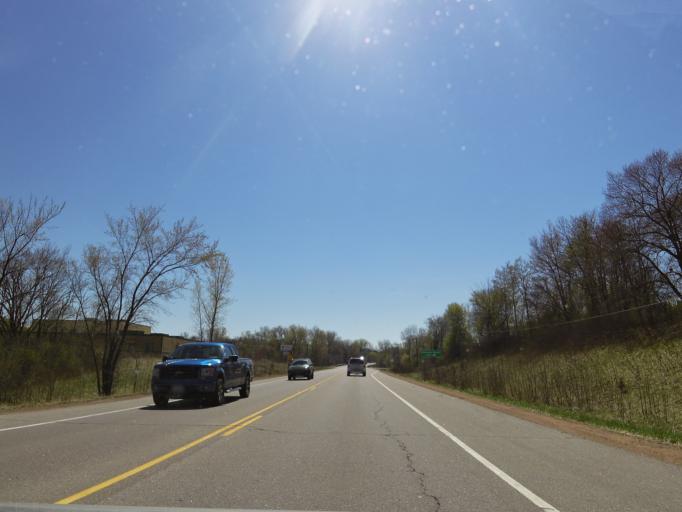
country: US
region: Minnesota
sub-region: Scott County
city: Prior Lake
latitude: 44.7362
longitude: -93.3847
